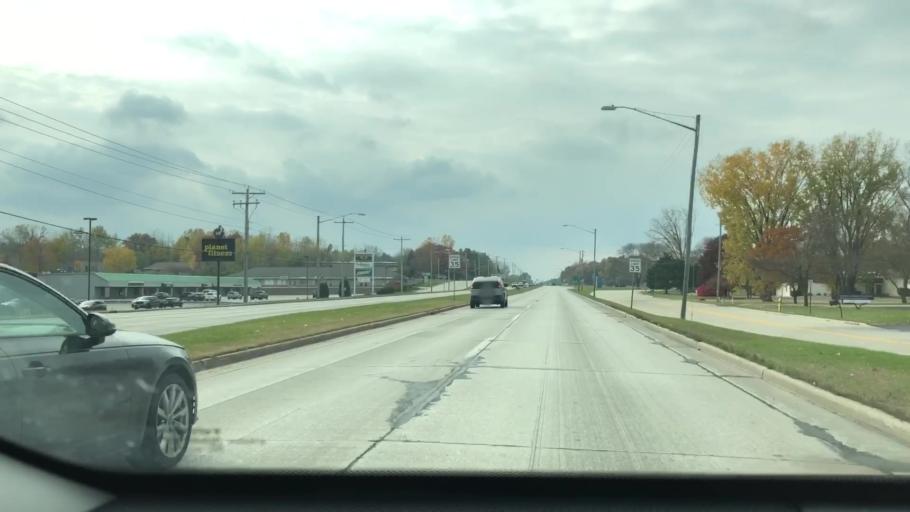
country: US
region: Wisconsin
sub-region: Brown County
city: Howard
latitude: 44.5240
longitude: -88.1001
